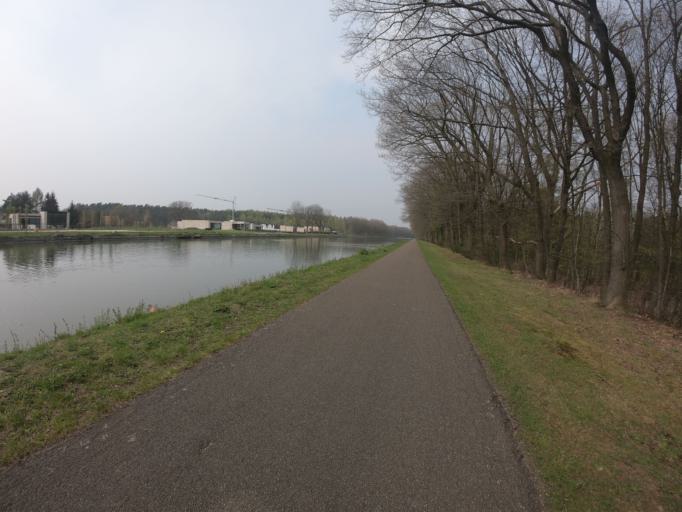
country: BE
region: Flanders
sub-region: Provincie Limburg
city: Maasmechelen
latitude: 51.0238
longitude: 5.7116
